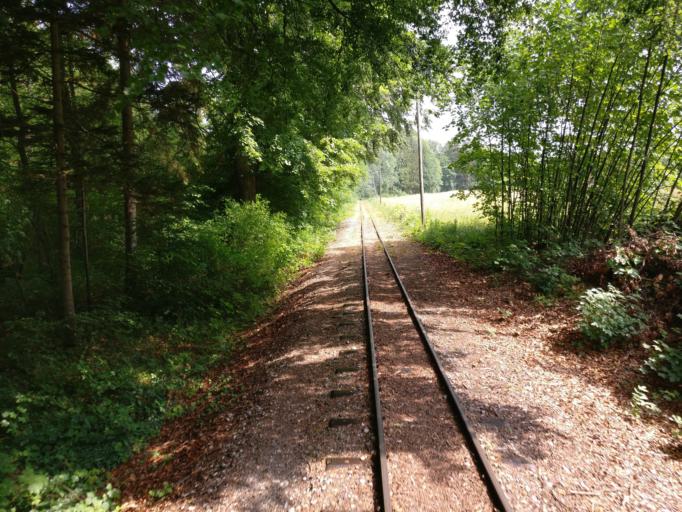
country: AT
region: Upper Austria
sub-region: Politischer Bezirk Steyr-Land
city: Sierning
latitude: 48.0489
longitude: 14.3395
